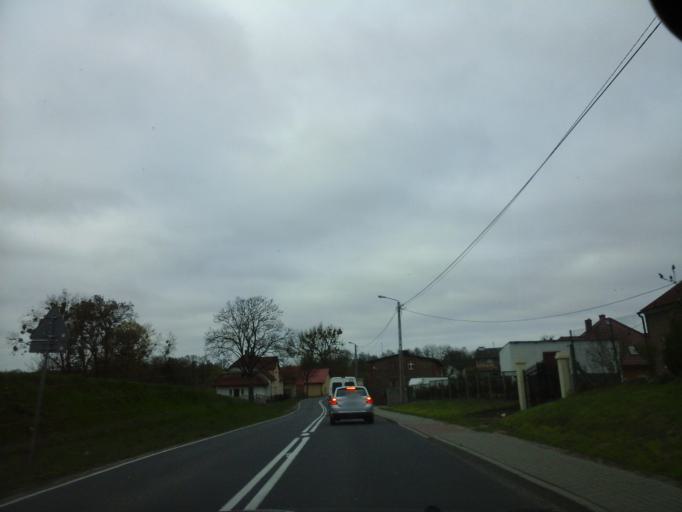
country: PL
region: West Pomeranian Voivodeship
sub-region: Powiat stargardzki
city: Suchan
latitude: 53.2316
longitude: 15.2998
